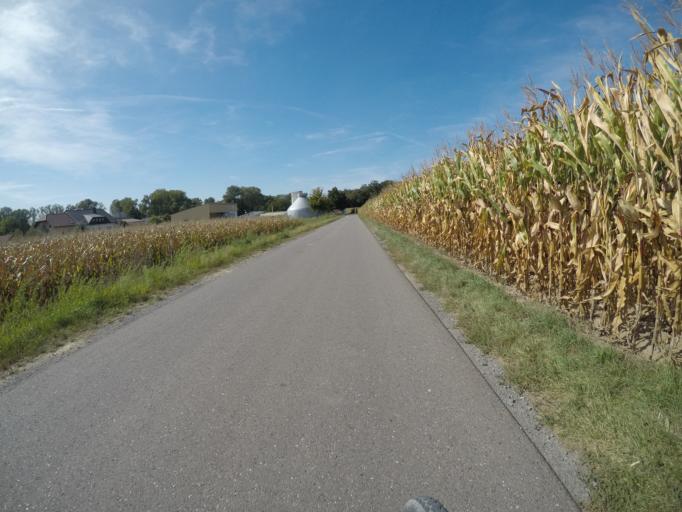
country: DE
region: Baden-Wuerttemberg
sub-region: Karlsruhe Region
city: Ubstadt-Weiher
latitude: 49.1519
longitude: 8.6541
